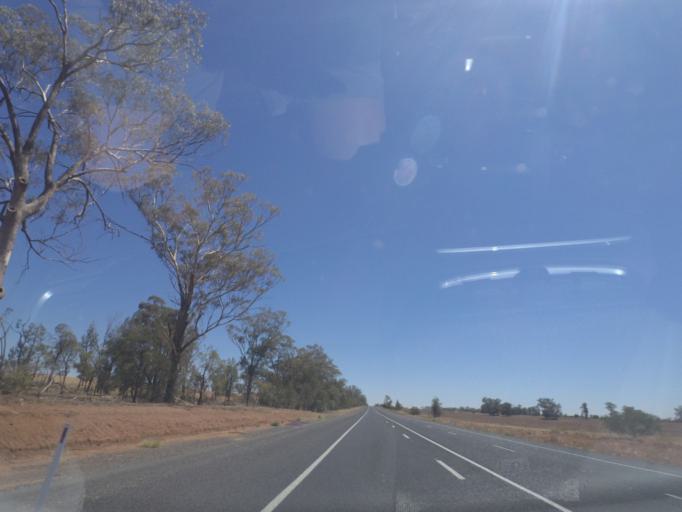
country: AU
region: New South Wales
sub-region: Gilgandra
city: Gilgandra
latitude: -31.4910
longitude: 148.8716
